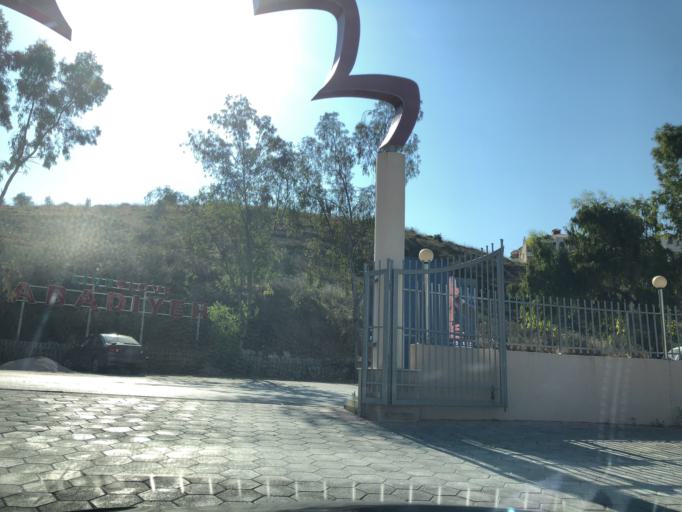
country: LB
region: Mont-Liban
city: Aaley
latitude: 33.8186
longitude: 35.6152
